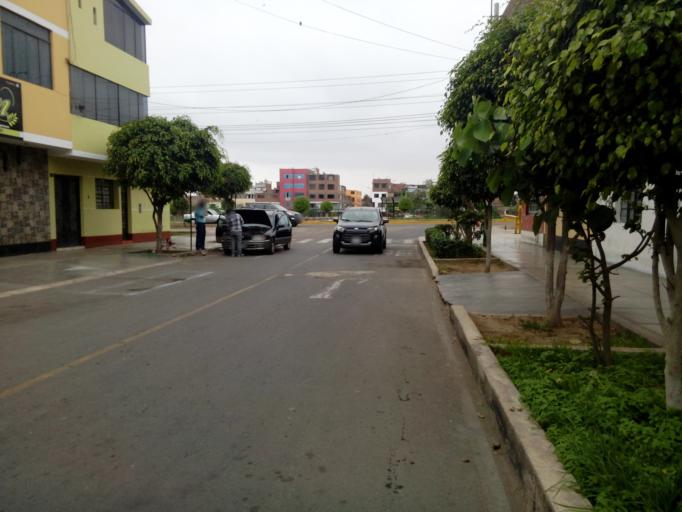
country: PE
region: Callao
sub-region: Callao
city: Callao
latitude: -12.0396
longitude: -77.0943
